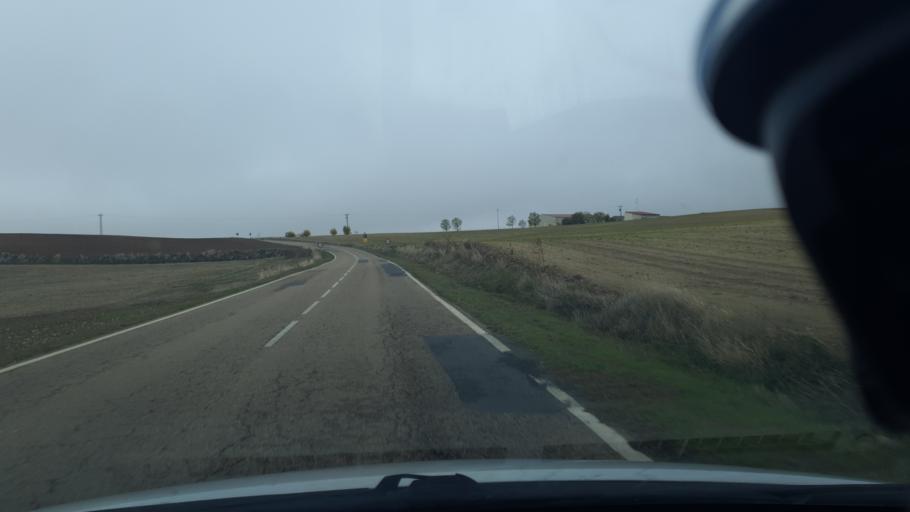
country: ES
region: Castille and Leon
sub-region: Provincia de Segovia
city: Hontanares de Eresma
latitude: 40.9925
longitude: -4.1929
